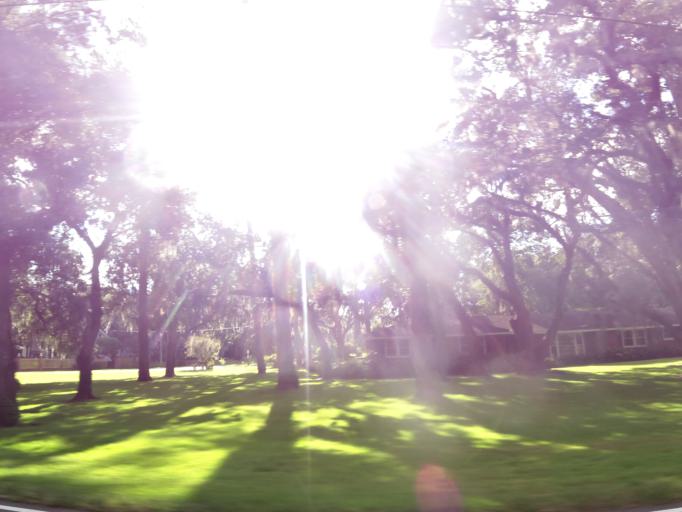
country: US
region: Georgia
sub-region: Glynn County
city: Saint Simons Island
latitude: 31.1749
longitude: -81.3779
